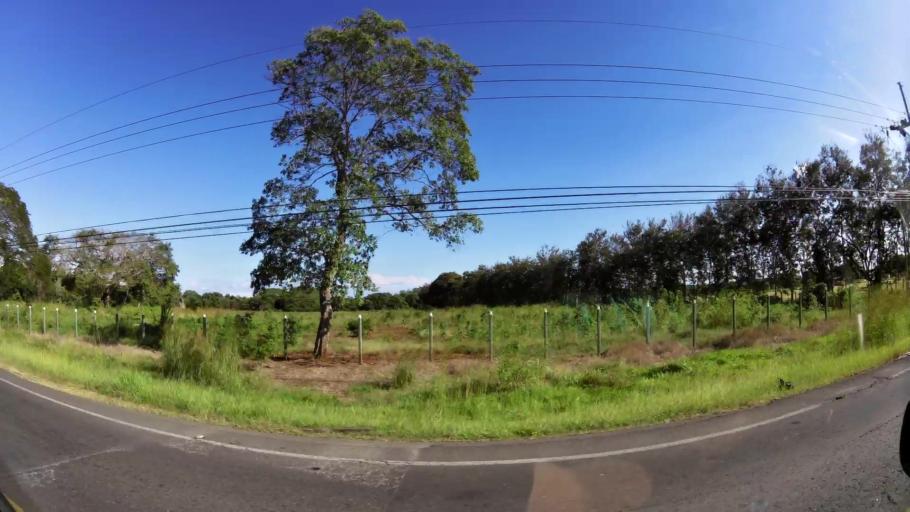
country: CR
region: Guanacaste
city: Sardinal
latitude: 10.5743
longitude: -85.5825
